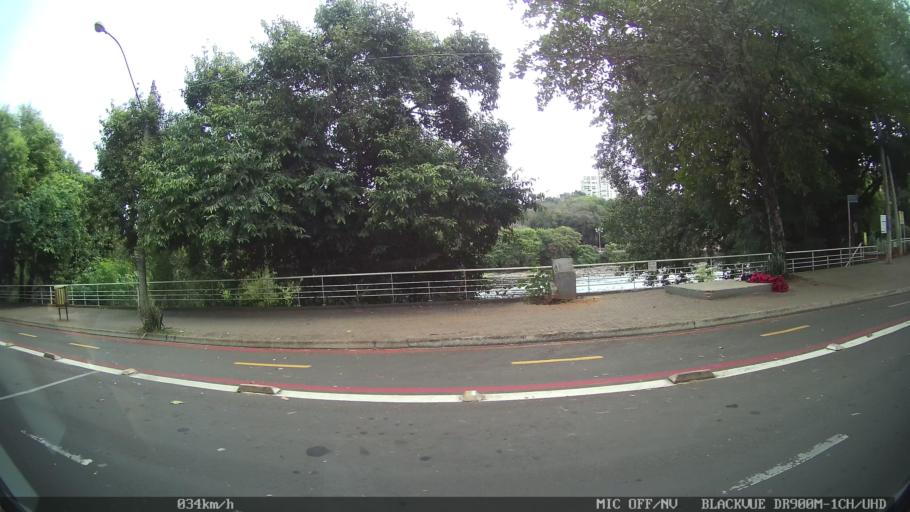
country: BR
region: Sao Paulo
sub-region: Piracicaba
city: Piracicaba
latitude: -22.7208
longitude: -47.6550
